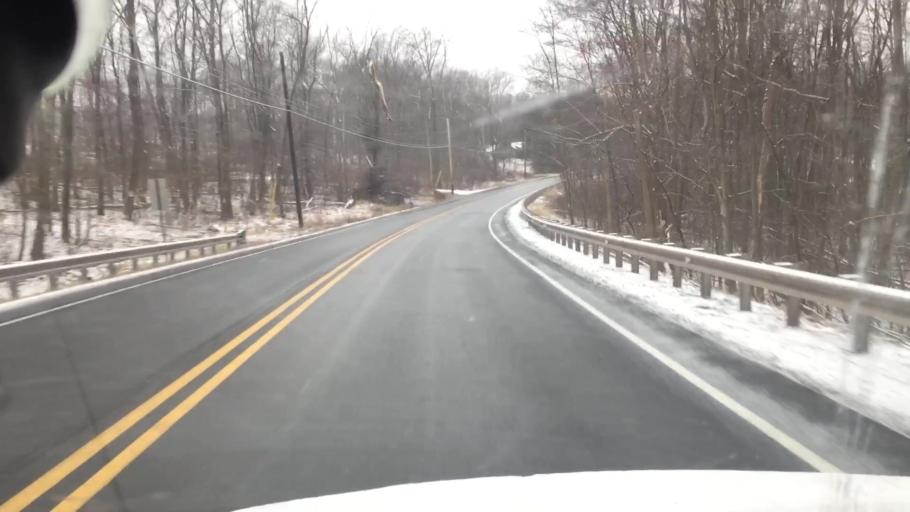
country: US
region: Pennsylvania
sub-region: Luzerne County
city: Conyngham
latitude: 41.0317
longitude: -76.1273
